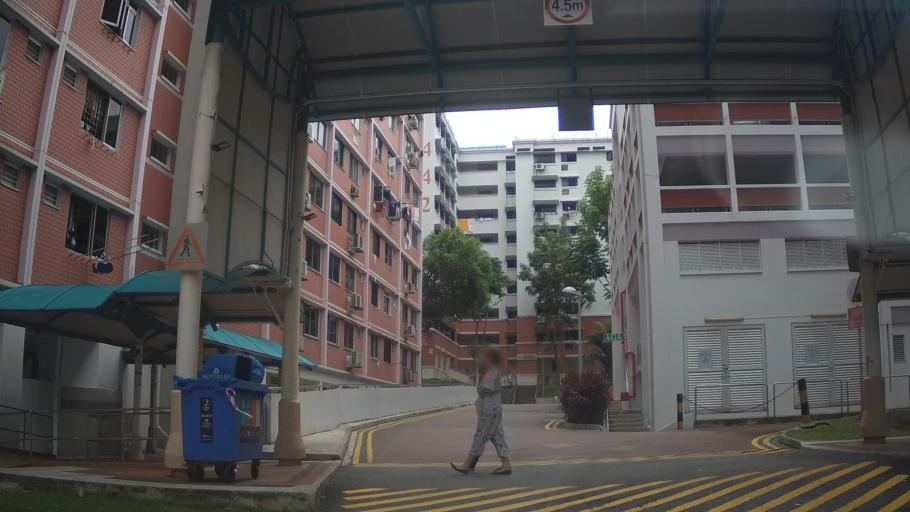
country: MY
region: Johor
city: Johor Bahru
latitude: 1.3829
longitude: 103.7707
